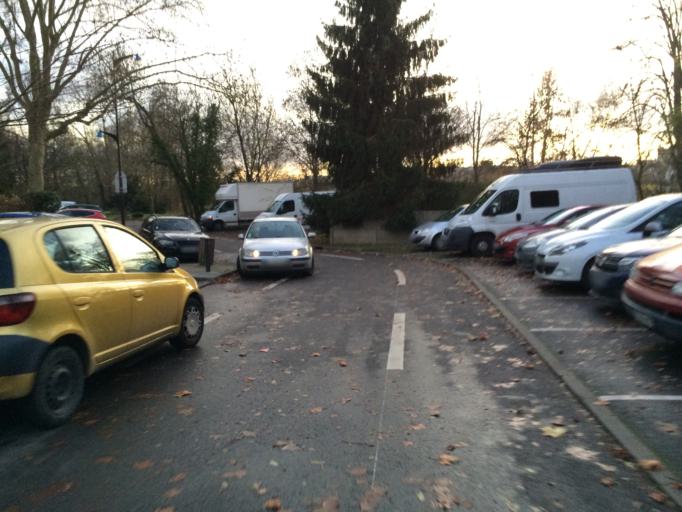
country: FR
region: Ile-de-France
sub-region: Departement de l'Essonne
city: Longjumeau
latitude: 48.6941
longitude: 2.3060
